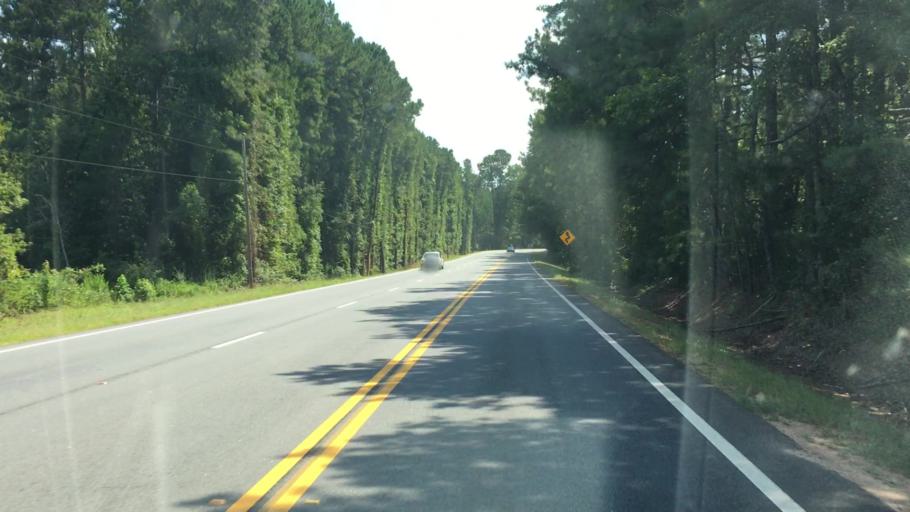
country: US
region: Georgia
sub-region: Oconee County
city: Watkinsville
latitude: 33.7298
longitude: -83.4307
